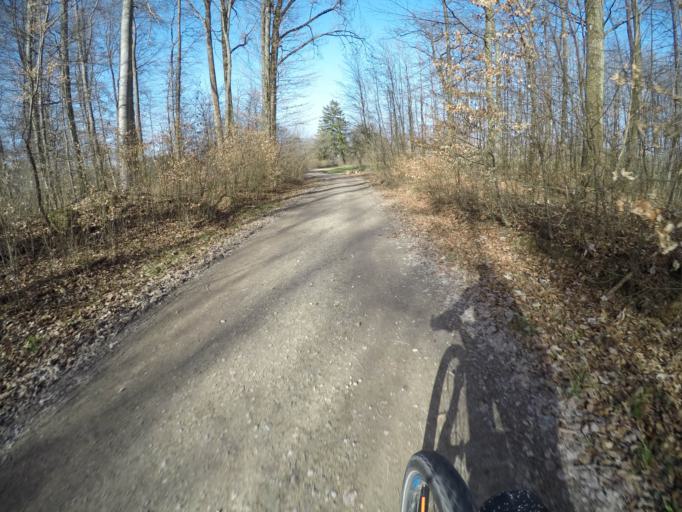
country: DE
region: Baden-Wuerttemberg
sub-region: Regierungsbezirk Stuttgart
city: Hochdorf
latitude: 48.6829
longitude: 9.4652
